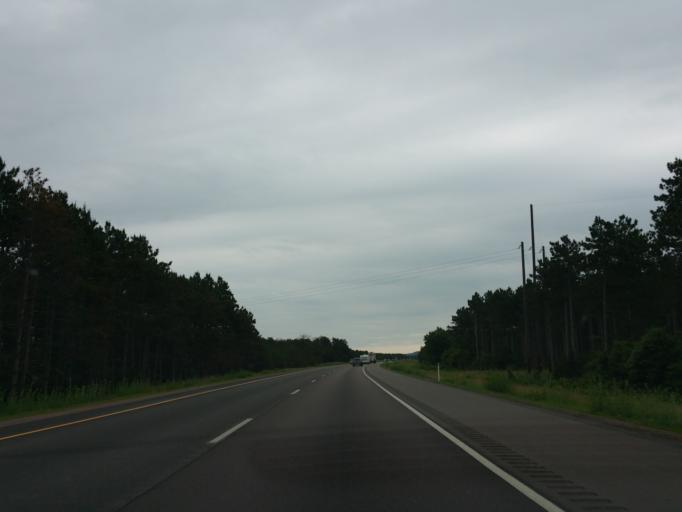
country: US
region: Wisconsin
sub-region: Trempealeau County
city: Osseo
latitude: 44.5618
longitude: -91.1831
